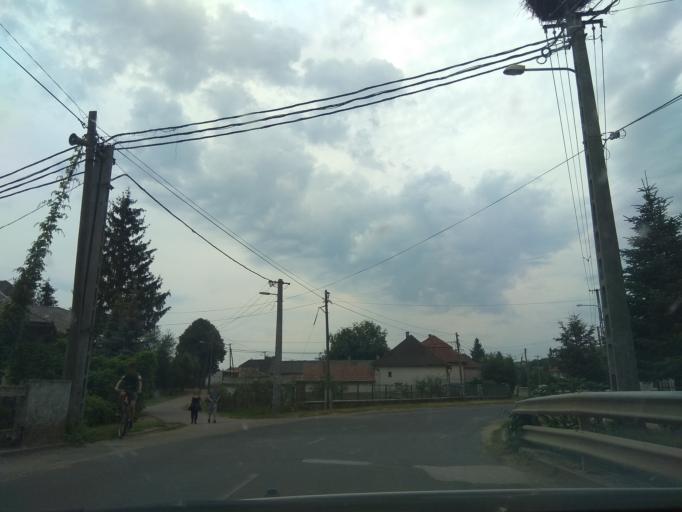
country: HU
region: Heves
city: Petervasara
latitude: 48.0401
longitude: 20.1028
